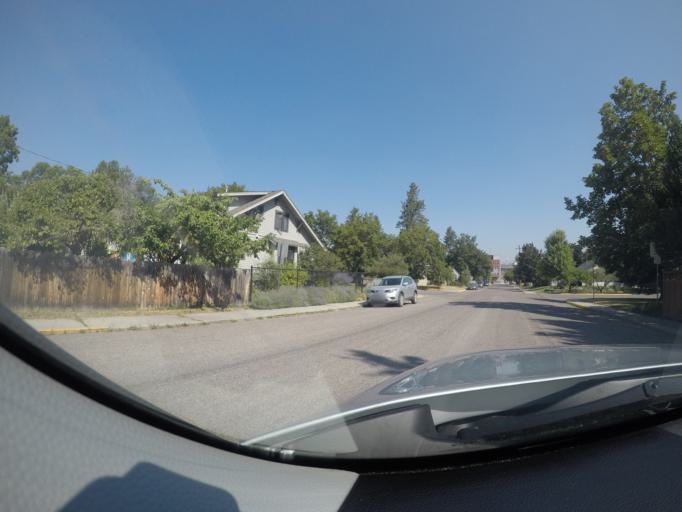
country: US
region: Montana
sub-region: Missoula County
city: Missoula
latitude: 46.8558
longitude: -113.9854
